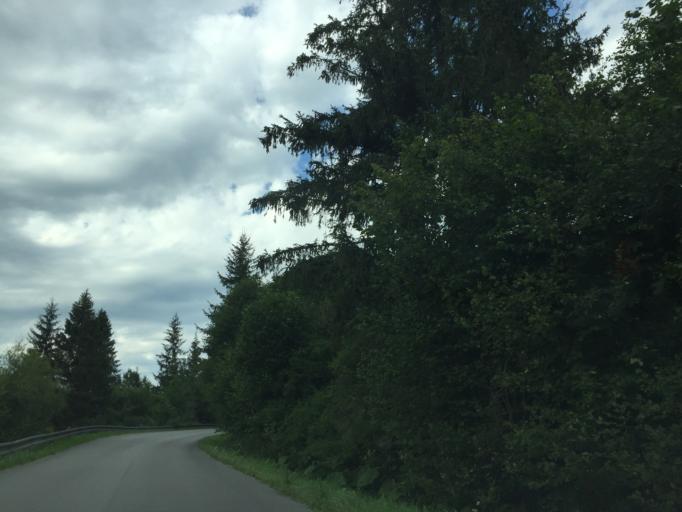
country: SK
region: Zilinsky
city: Namestovo
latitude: 49.4052
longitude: 19.3323
